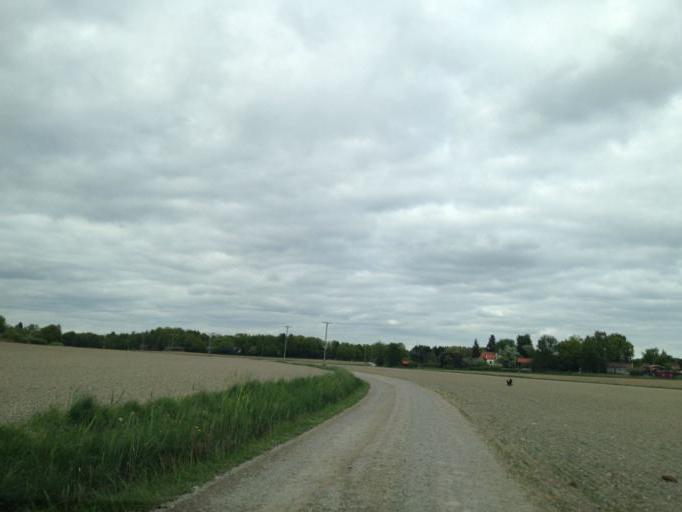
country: SE
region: Soedermanland
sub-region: Eskilstuna Kommun
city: Kvicksund
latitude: 59.4402
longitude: 16.3022
